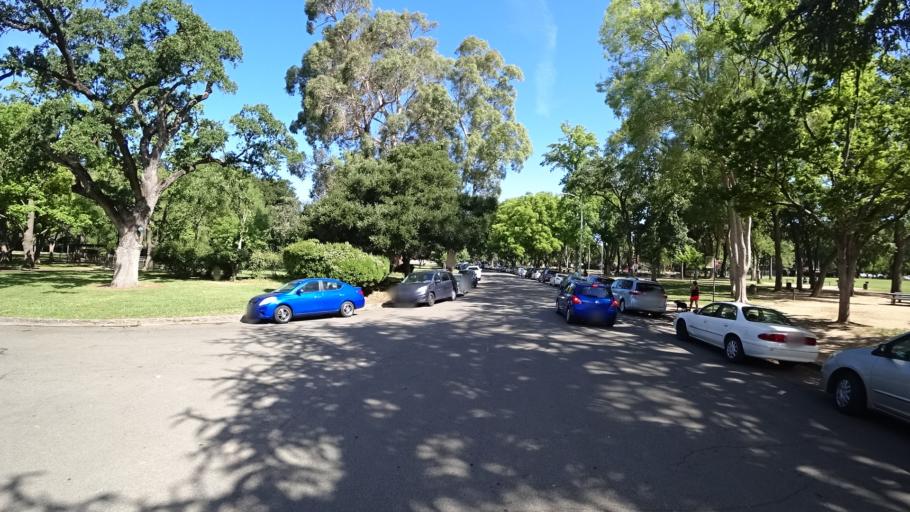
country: US
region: California
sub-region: Sacramento County
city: Sacramento
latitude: 38.5378
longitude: -121.5016
